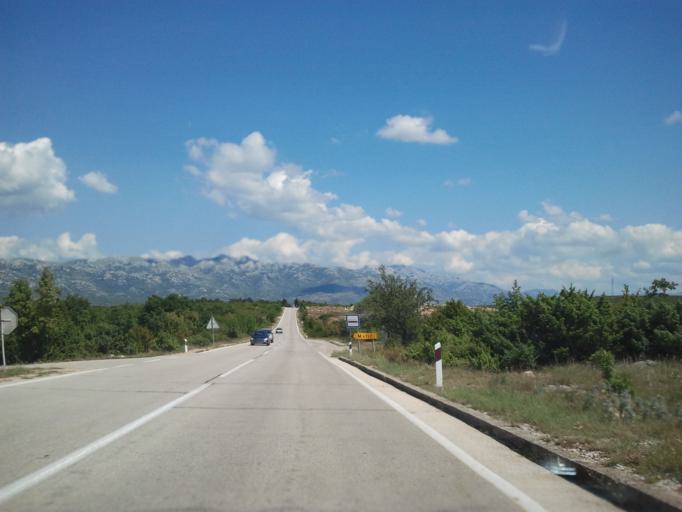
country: HR
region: Zadarska
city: Krusevo
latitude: 44.1927
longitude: 15.6433
